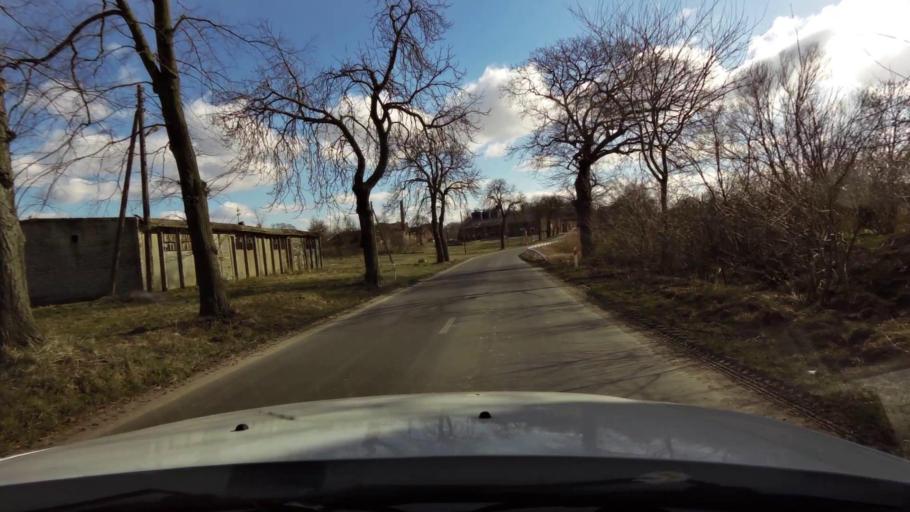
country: PL
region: West Pomeranian Voivodeship
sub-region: Powiat choszczenski
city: Pelczyce
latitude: 53.0937
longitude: 15.2968
